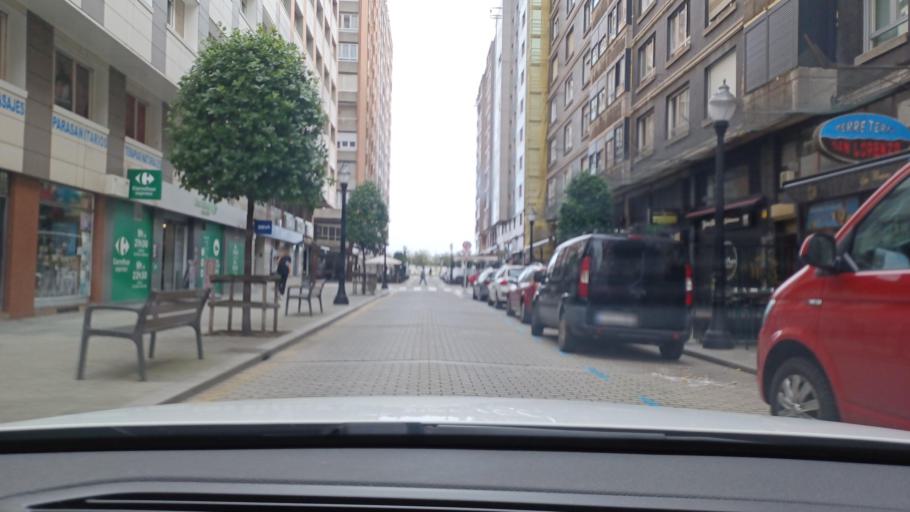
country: ES
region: Asturias
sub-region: Province of Asturias
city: Gijon
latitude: 43.5391
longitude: -5.6489
